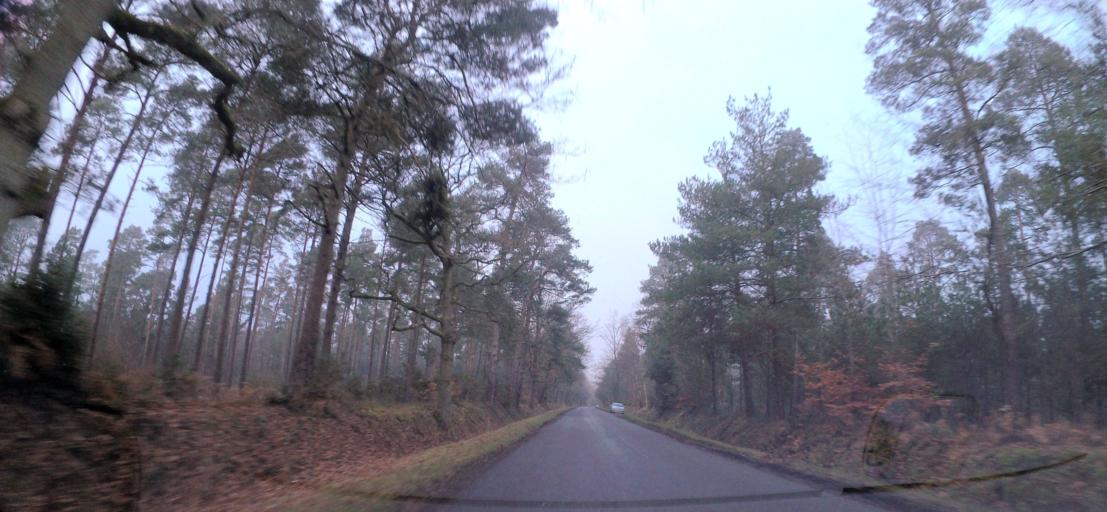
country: GB
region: England
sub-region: West Berkshire
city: Theale
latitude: 51.3857
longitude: -1.0883
